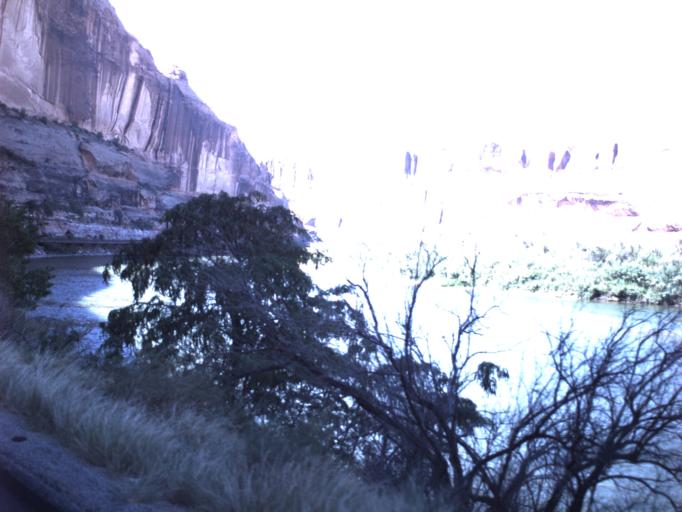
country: US
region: Utah
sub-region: Grand County
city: Moab
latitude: 38.6074
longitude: -109.5421
